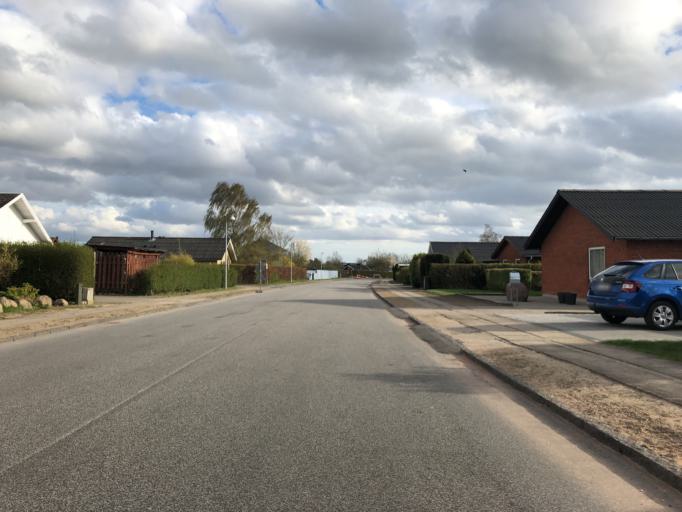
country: DK
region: Zealand
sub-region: Ringsted Kommune
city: Ringsted
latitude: 55.4410
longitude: 11.8046
